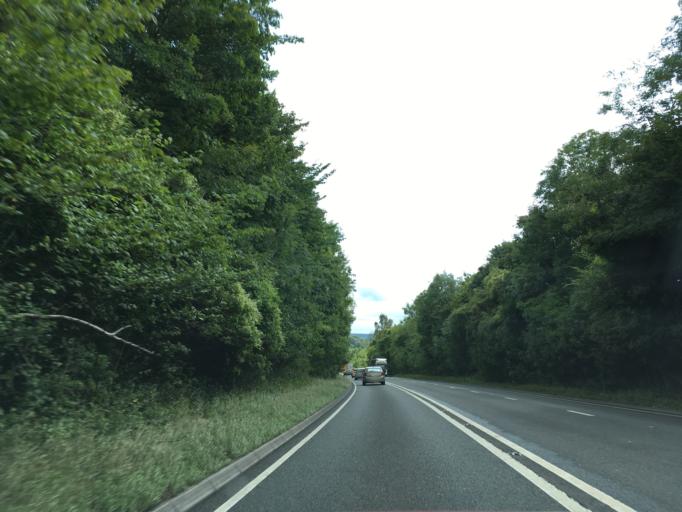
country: GB
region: England
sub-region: South Gloucestershire
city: Cold Ashton
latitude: 51.4179
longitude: -2.3506
